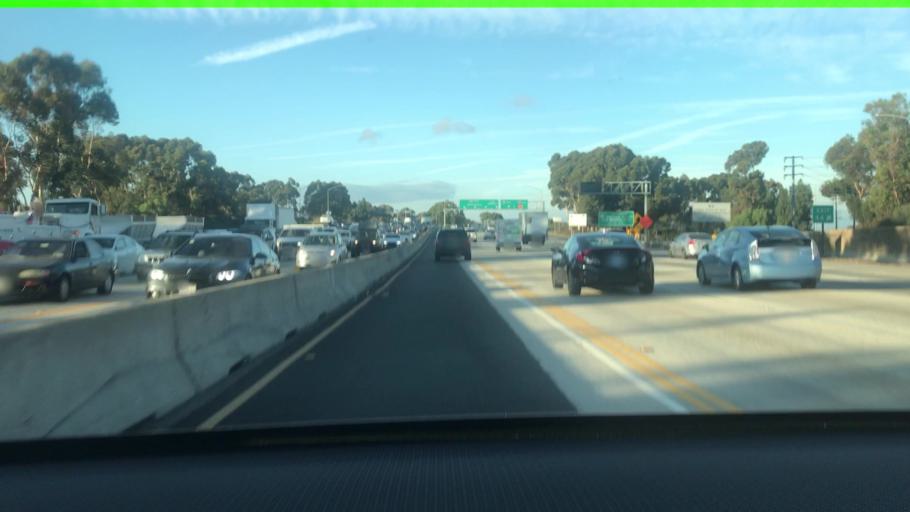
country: US
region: California
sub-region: Los Angeles County
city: Del Aire
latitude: 33.9131
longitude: -118.3698
